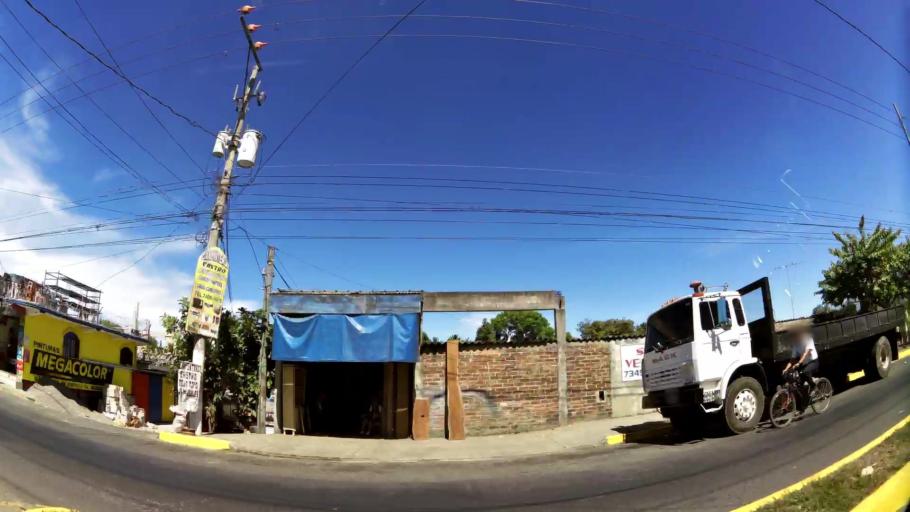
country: SV
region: La Libertad
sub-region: Distrito de Quezaltepeque
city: Quezaltepeque
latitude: 13.8312
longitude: -89.2698
